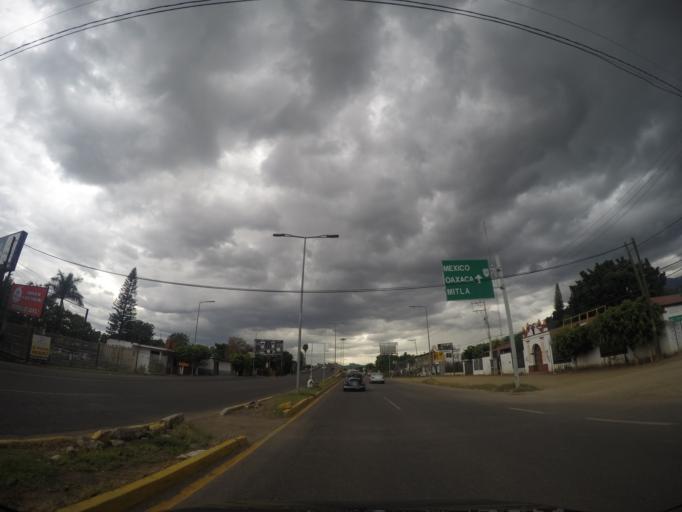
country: MX
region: Oaxaca
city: Tlalixtac de Cabrera
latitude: 17.0590
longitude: -96.6599
